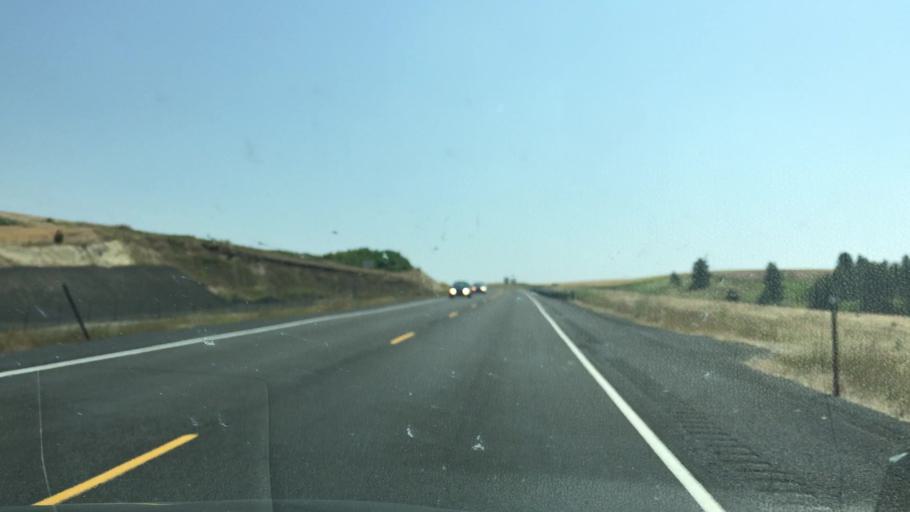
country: US
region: Idaho
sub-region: Lewis County
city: Nezperce
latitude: 46.2347
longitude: -116.5141
